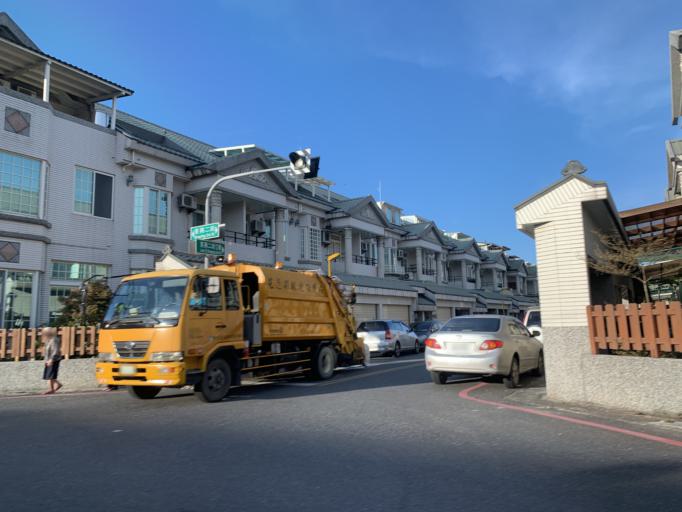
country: TW
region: Taiwan
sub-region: Hualien
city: Hualian
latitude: 23.9989
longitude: 121.6303
